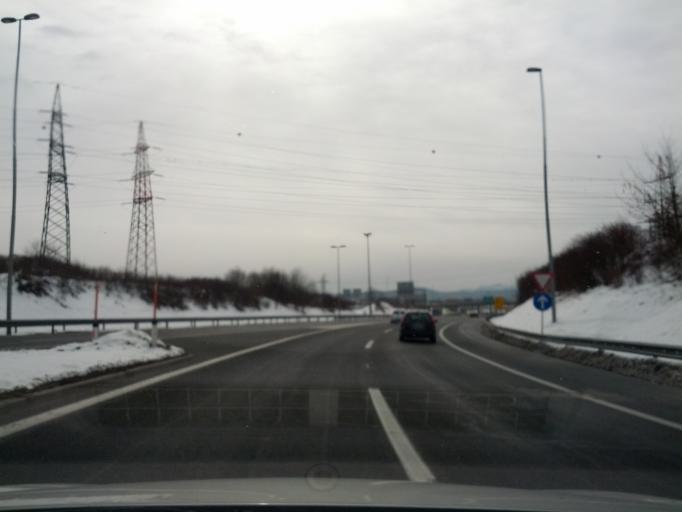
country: SI
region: Dol pri Ljubljani
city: Dol pri Ljubljani
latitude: 46.0658
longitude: 14.5756
